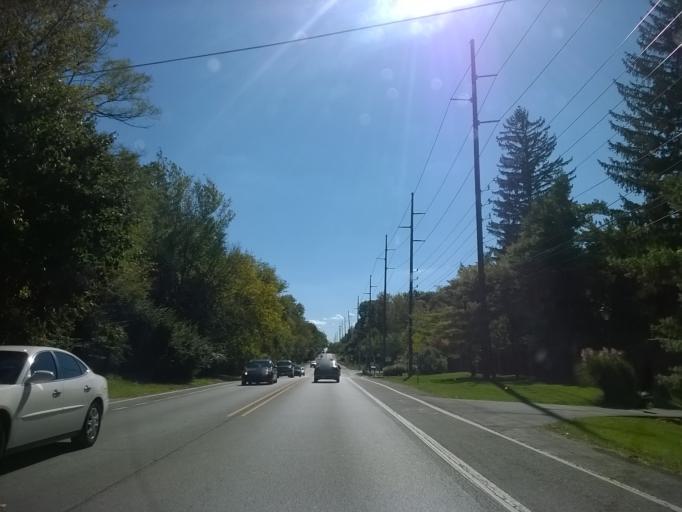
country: US
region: Indiana
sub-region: Marion County
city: Broad Ripple
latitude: 39.8918
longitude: -86.0856
